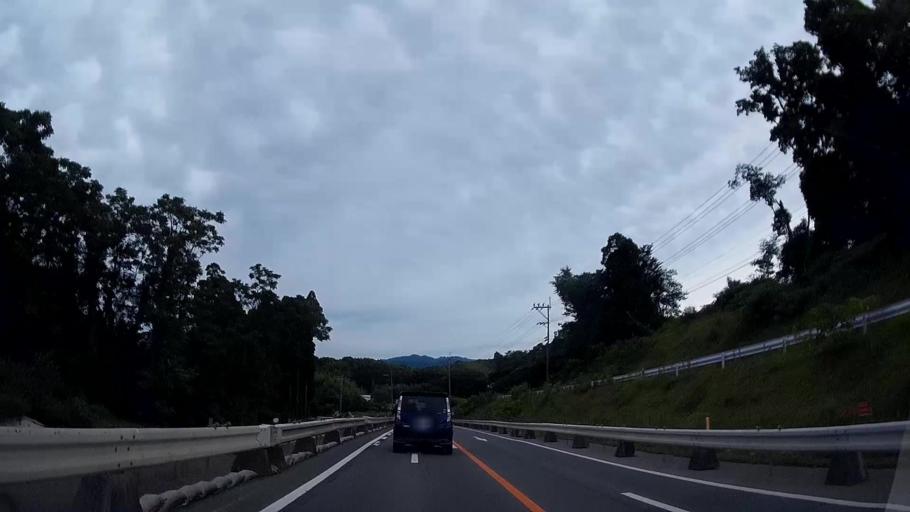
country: JP
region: Kumamoto
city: Kikuchi
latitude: 32.9504
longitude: 130.8243
